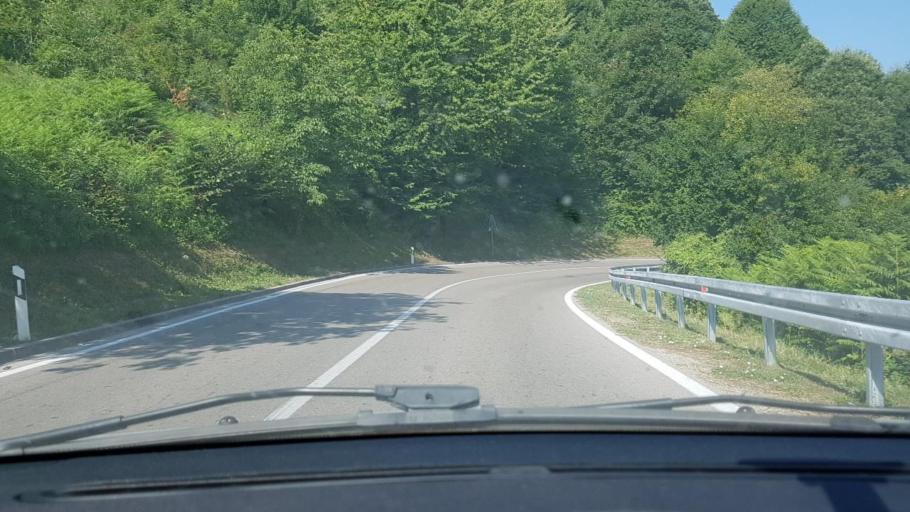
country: BA
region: Federation of Bosnia and Herzegovina
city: Pecigrad
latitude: 45.0502
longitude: 15.9021
